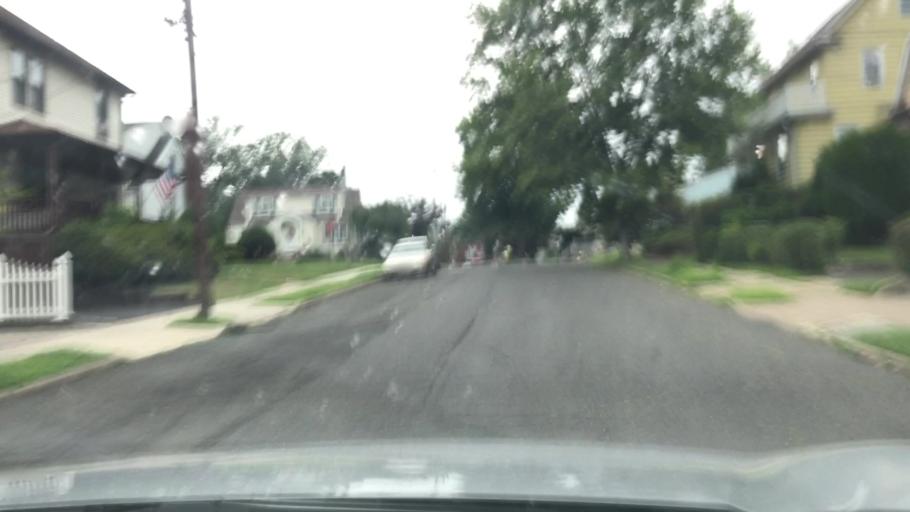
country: US
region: New Jersey
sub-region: Bergen County
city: Bergenfield
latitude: 40.9232
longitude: -74.0040
